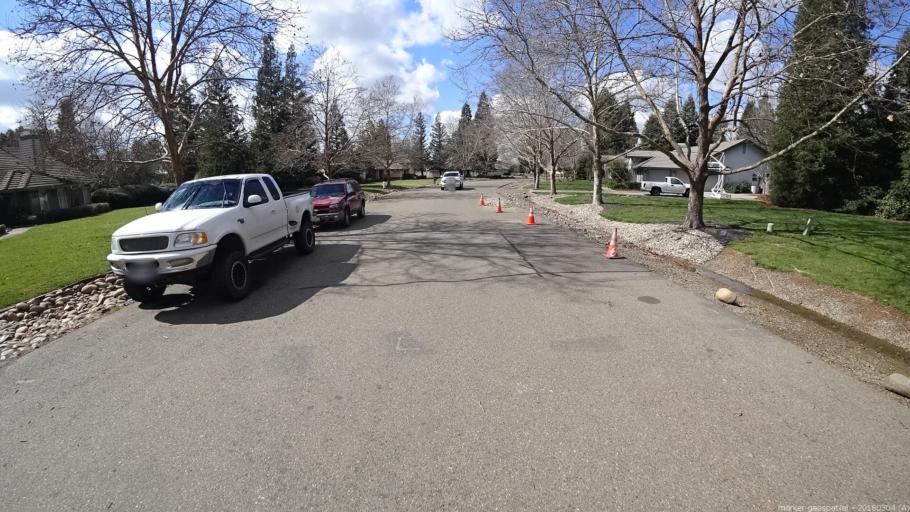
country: US
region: California
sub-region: Sacramento County
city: Vineyard
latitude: 38.4535
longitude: -121.3130
